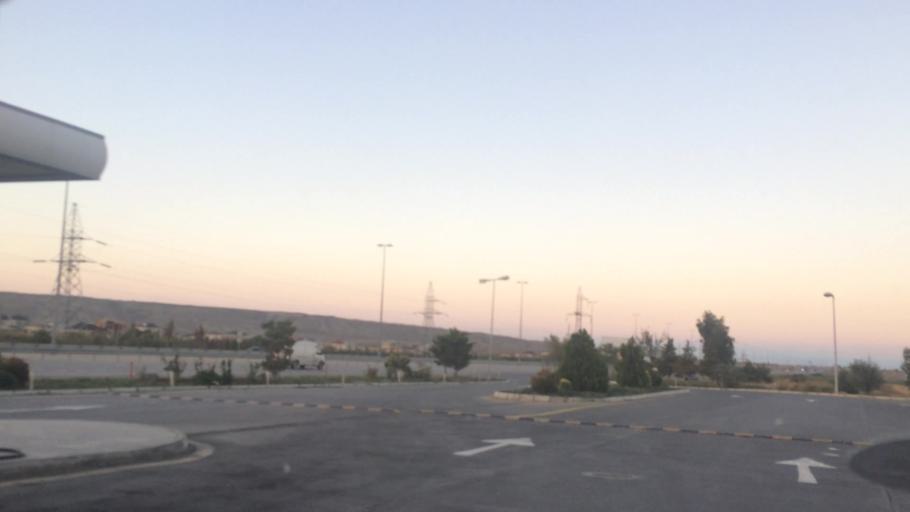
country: AZ
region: Baki
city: Qobustan
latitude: 39.9703
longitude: 49.4156
